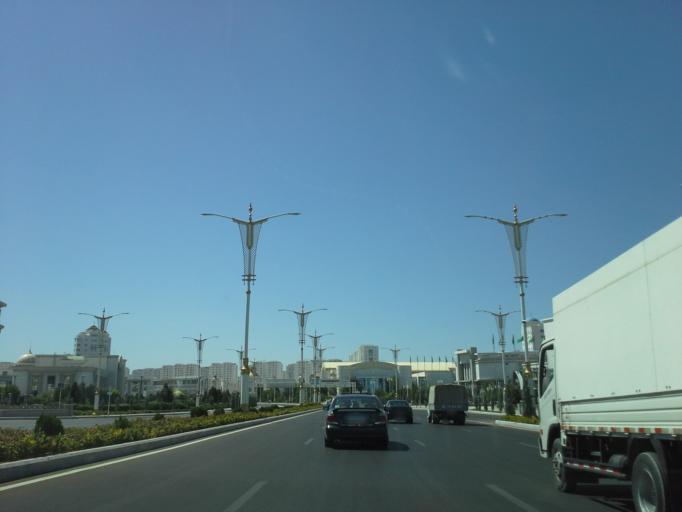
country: TM
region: Ahal
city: Ashgabat
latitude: 37.9144
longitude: 58.3779
